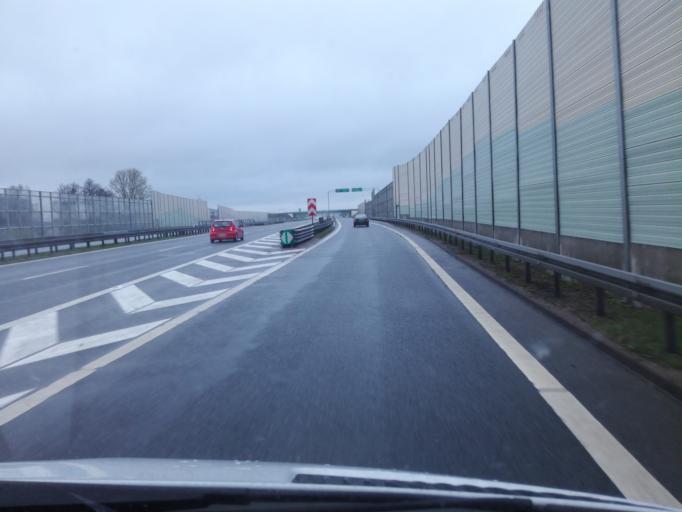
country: PL
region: Podlasie
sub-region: Powiat zambrowski
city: Zambrow
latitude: 52.9746
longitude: 22.2094
